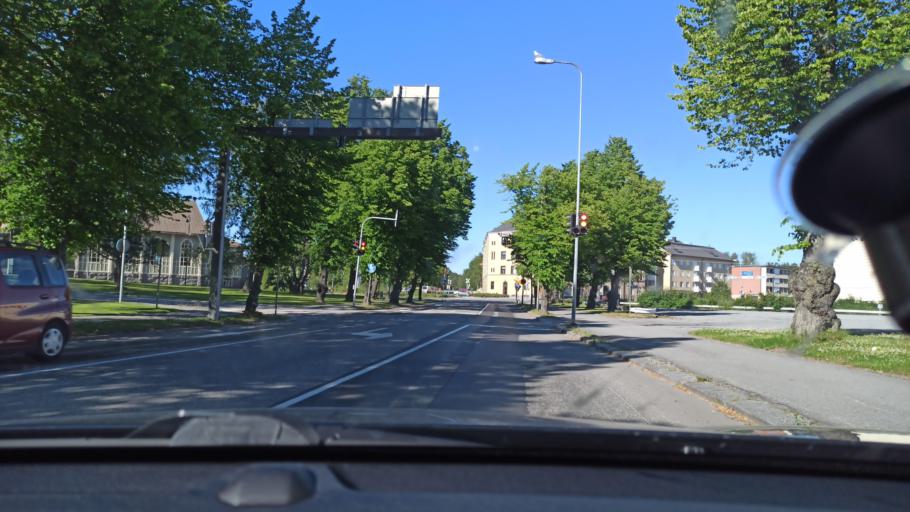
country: FI
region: Ostrobothnia
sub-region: Jakobstadsregionen
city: Jakobstad
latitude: 63.6770
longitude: 22.7109
